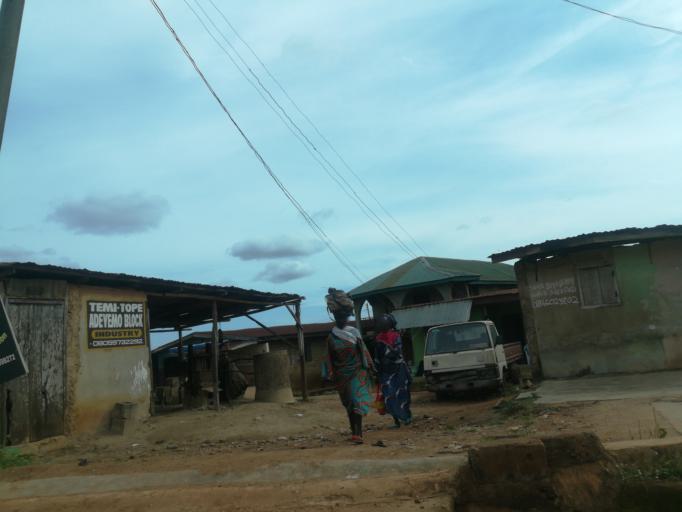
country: NG
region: Oyo
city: Ibadan
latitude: 7.3771
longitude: 3.9587
